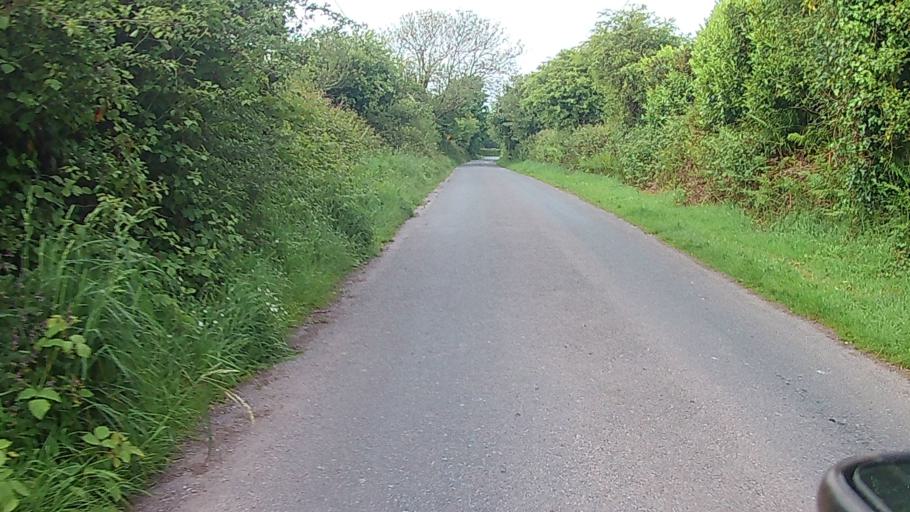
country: IE
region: Munster
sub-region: County Cork
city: Watergrasshill
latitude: 51.9935
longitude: -8.3958
